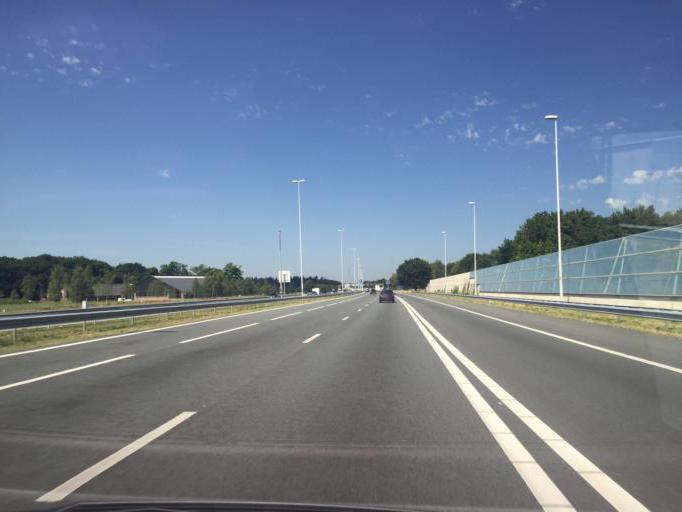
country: NL
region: Utrecht
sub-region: Gemeente Utrechtse Heuvelrug
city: Maarsbergen
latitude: 52.0568
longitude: 5.3966
